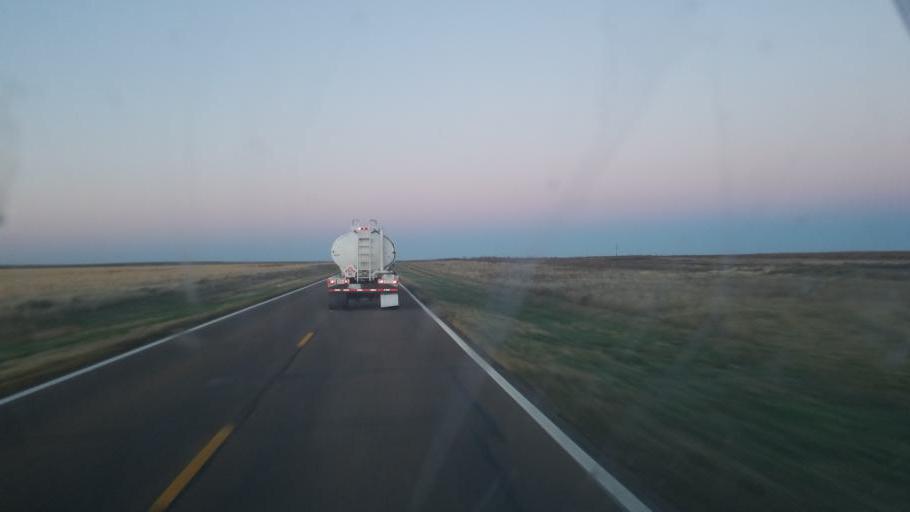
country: US
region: Kansas
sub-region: Wallace County
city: Sharon Springs
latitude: 38.9401
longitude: -101.5180
